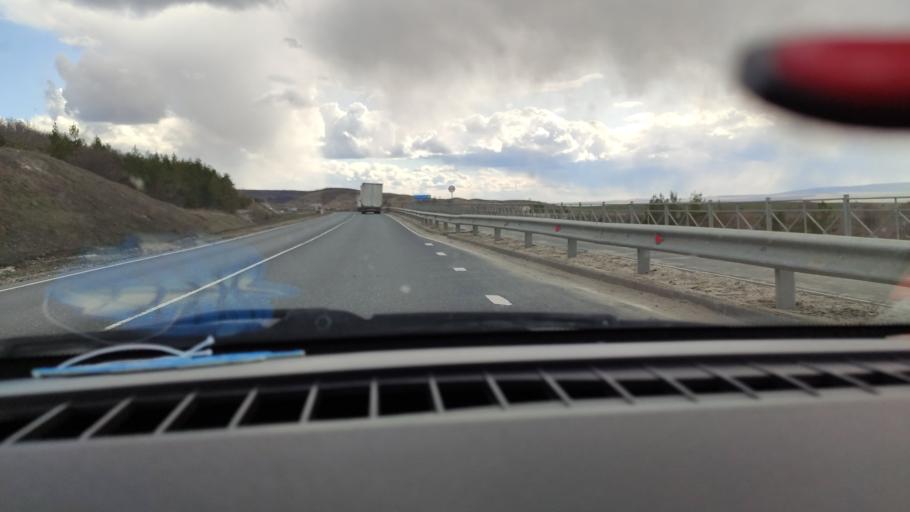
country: RU
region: Saratov
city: Alekseyevka
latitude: 52.3847
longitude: 47.9741
